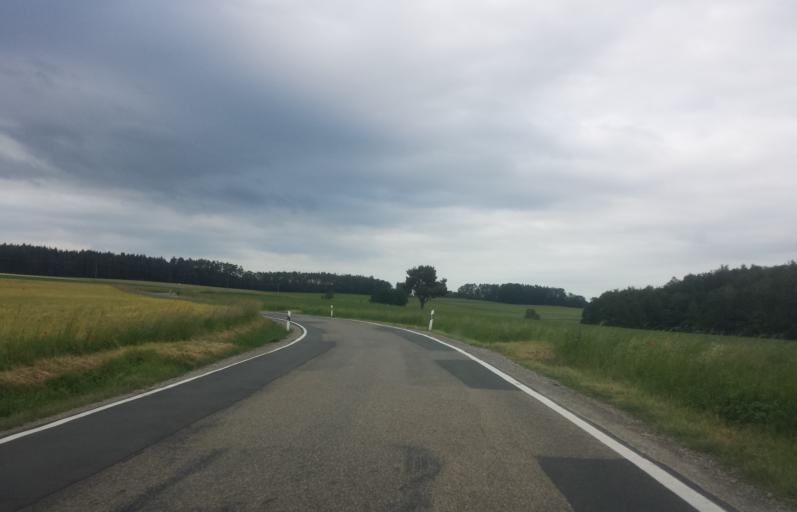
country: DE
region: Bavaria
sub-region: Regierungsbezirk Mittelfranken
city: Markt Taschendorf
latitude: 49.7012
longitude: 10.5891
